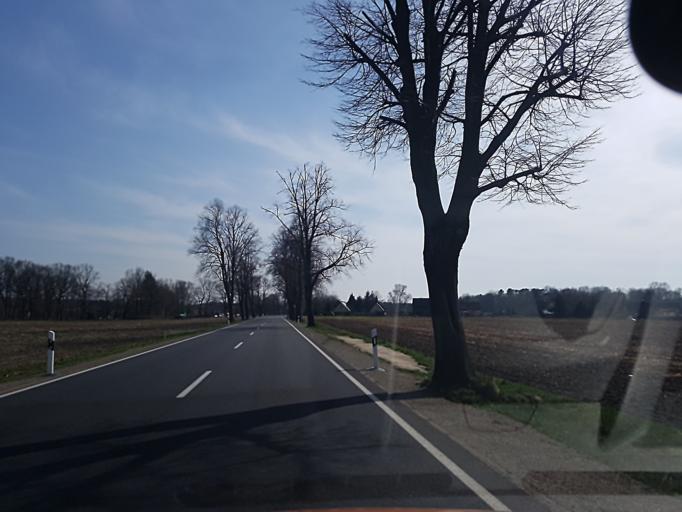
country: DE
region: Brandenburg
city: Bronkow
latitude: 51.6756
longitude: 13.9142
